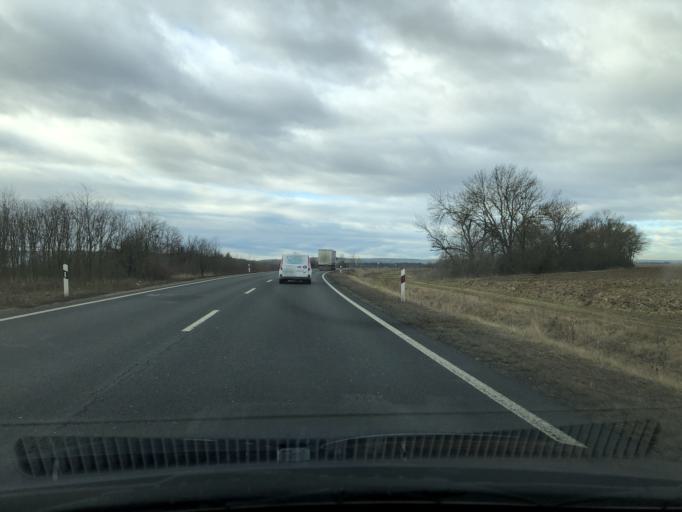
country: HU
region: Vas
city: Gencsapati
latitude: 47.2521
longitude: 16.5792
